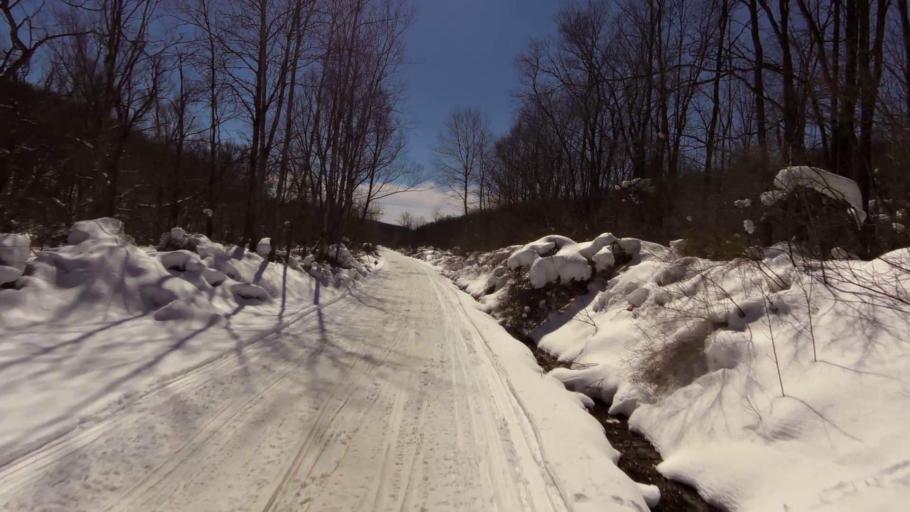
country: US
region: New York
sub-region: Cattaraugus County
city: Delevan
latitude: 42.4242
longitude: -78.4566
